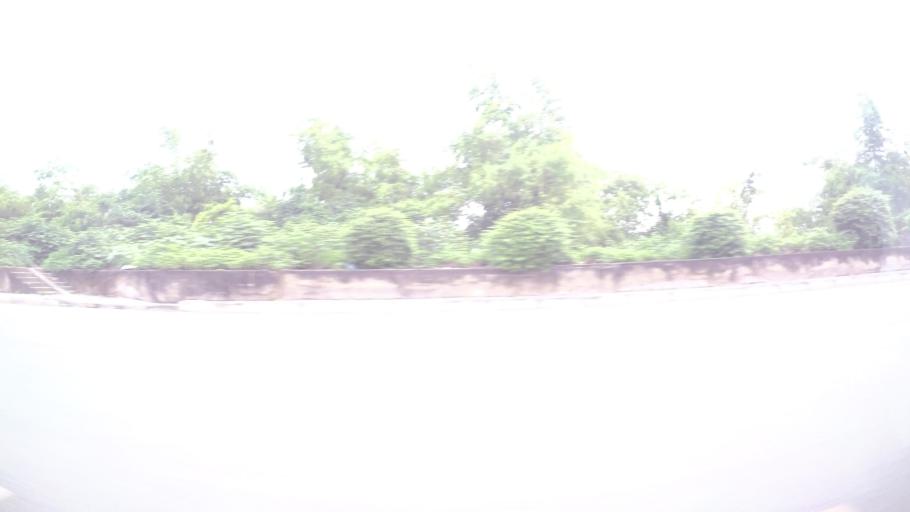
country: VN
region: Ha Noi
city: Trau Quy
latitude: 21.0769
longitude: 105.9015
